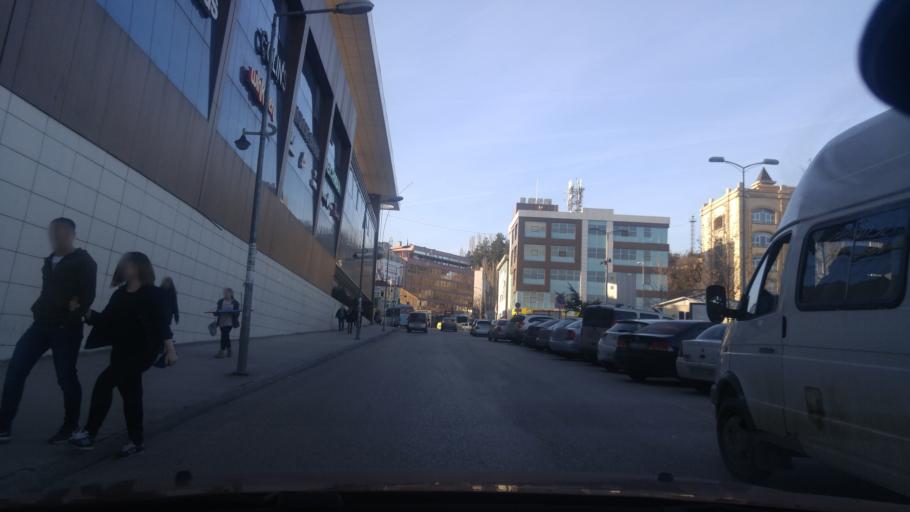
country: TR
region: Karabuk
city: Karabuk
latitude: 41.1961
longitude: 32.6182
